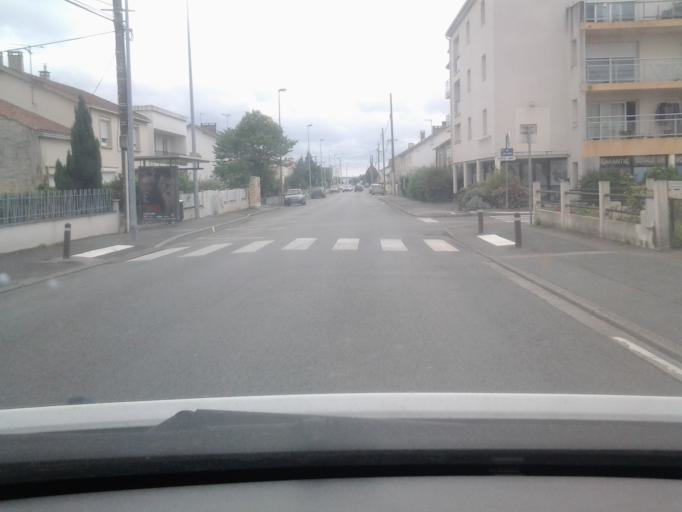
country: FR
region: Pays de la Loire
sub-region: Departement de la Vendee
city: La Roche-sur-Yon
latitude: 46.6559
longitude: -1.4323
